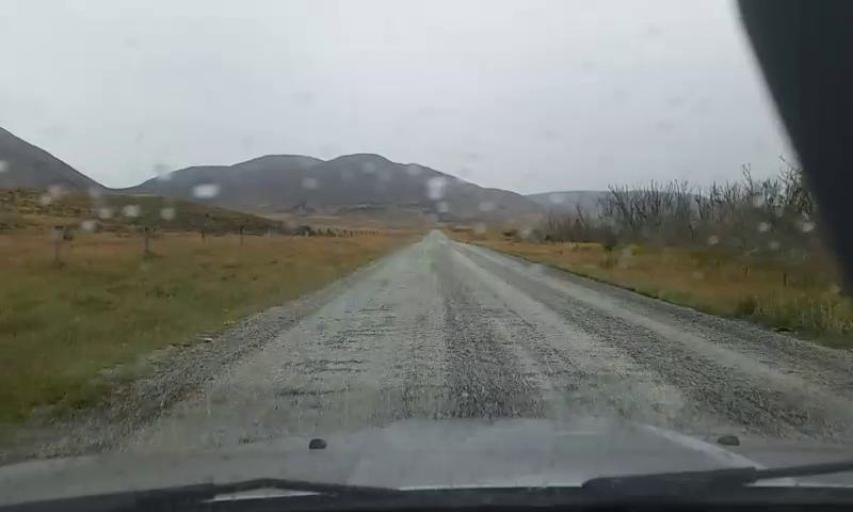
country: NZ
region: Canterbury
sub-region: Ashburton District
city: Methven
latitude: -43.6158
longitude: 171.0911
